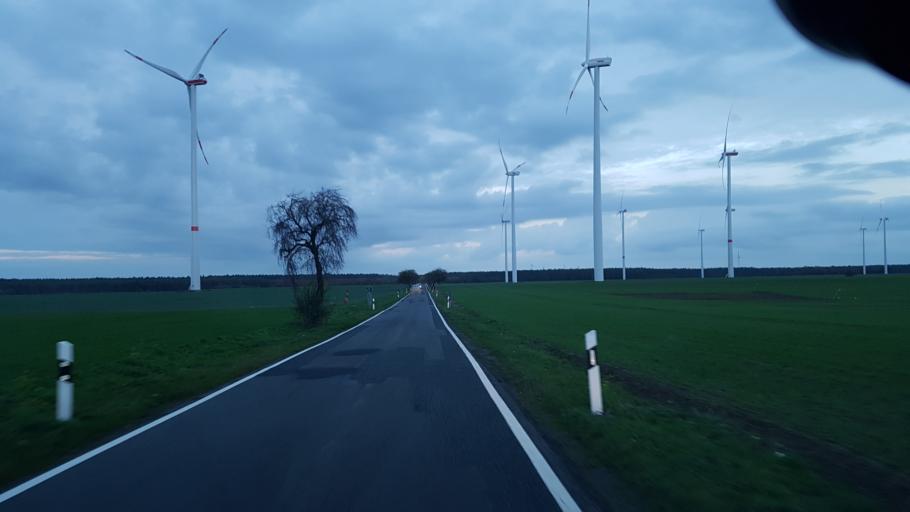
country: DE
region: Brandenburg
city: Muhlberg
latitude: 51.4631
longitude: 13.2499
